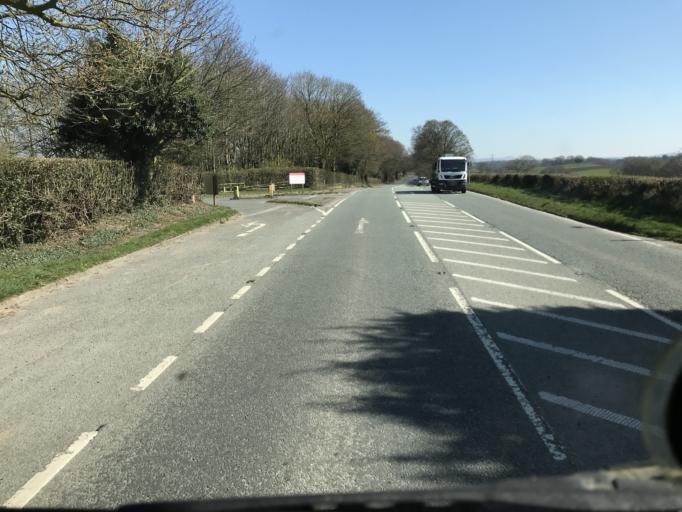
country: GB
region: England
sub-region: Cheshire East
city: Siddington
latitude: 53.2656
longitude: -2.2517
